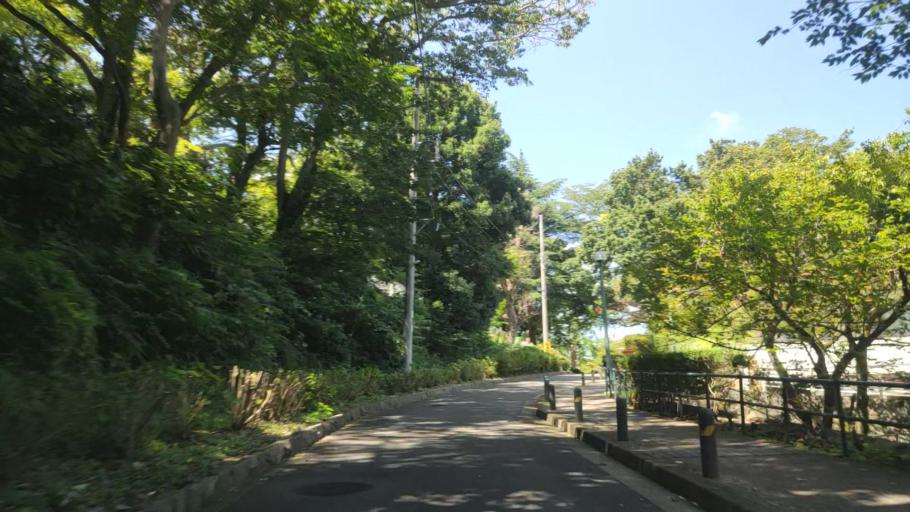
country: JP
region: Kanagawa
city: Yokohama
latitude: 35.5251
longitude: 139.6283
